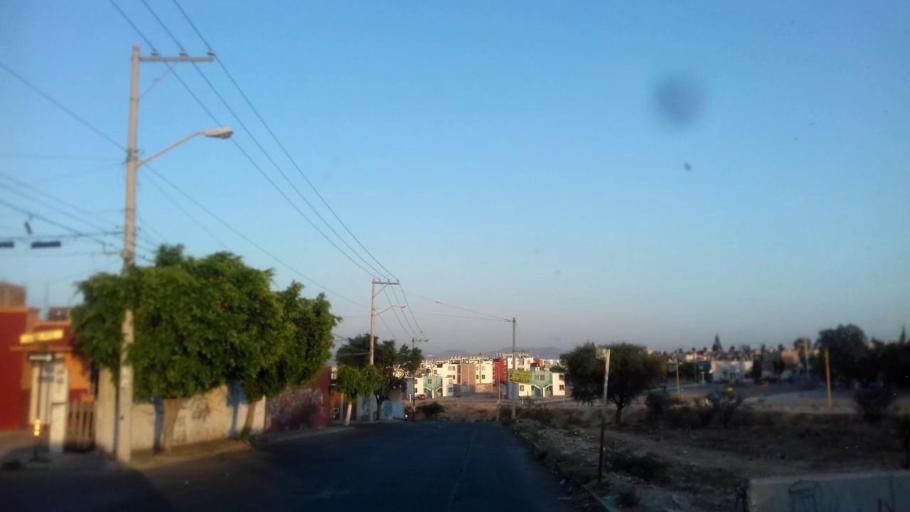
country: MX
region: Aguascalientes
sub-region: Aguascalientes
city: San Sebastian [Fraccionamiento]
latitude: 21.8502
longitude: -102.2575
